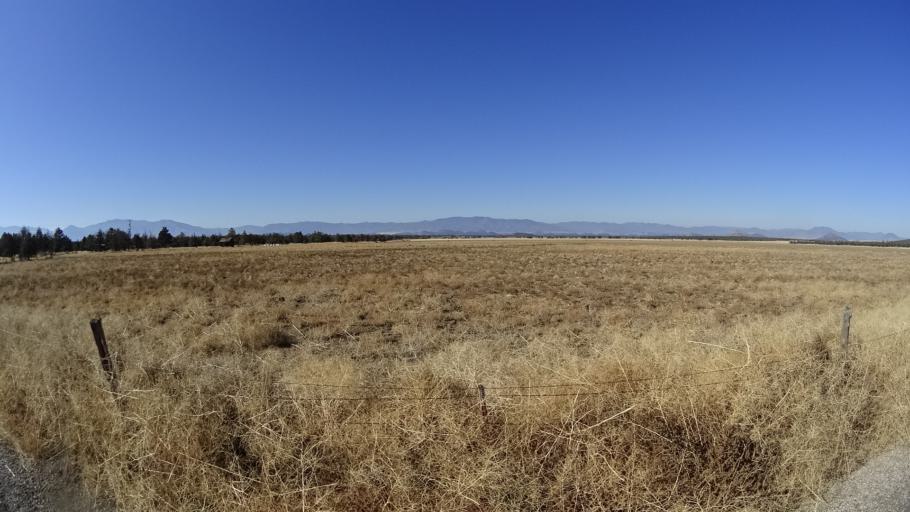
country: US
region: California
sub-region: Siskiyou County
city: Weed
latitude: 41.5953
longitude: -122.3019
